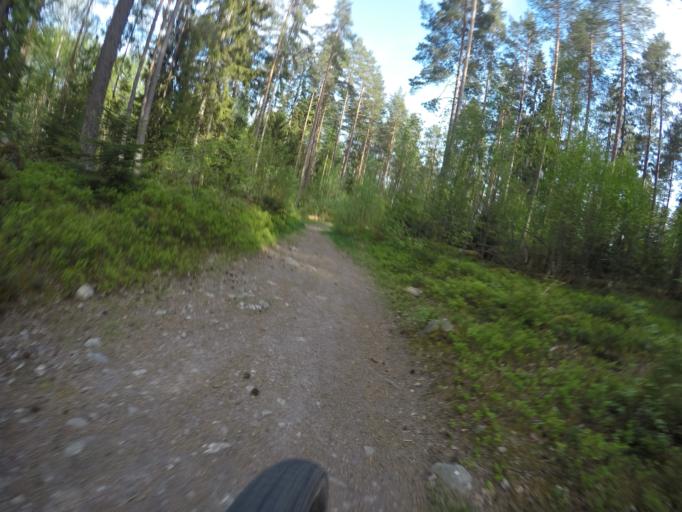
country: SE
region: Vaestmanland
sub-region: Vasteras
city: Vasteras
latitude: 59.6540
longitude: 16.5242
